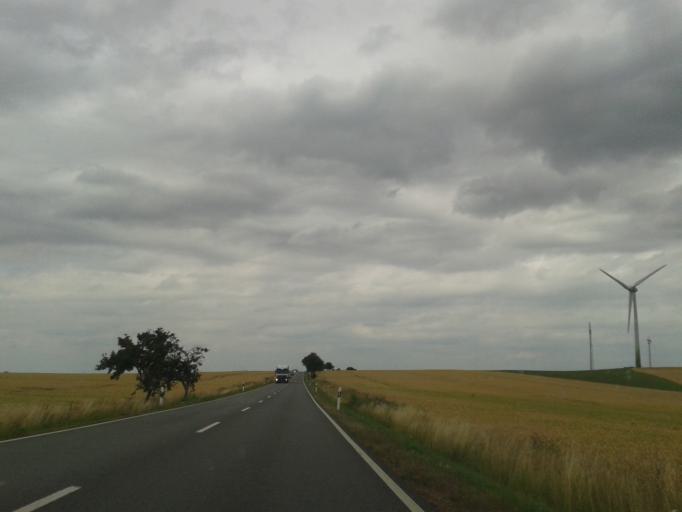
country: DE
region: Saxony
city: Niederschona
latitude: 50.9859
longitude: 13.4478
